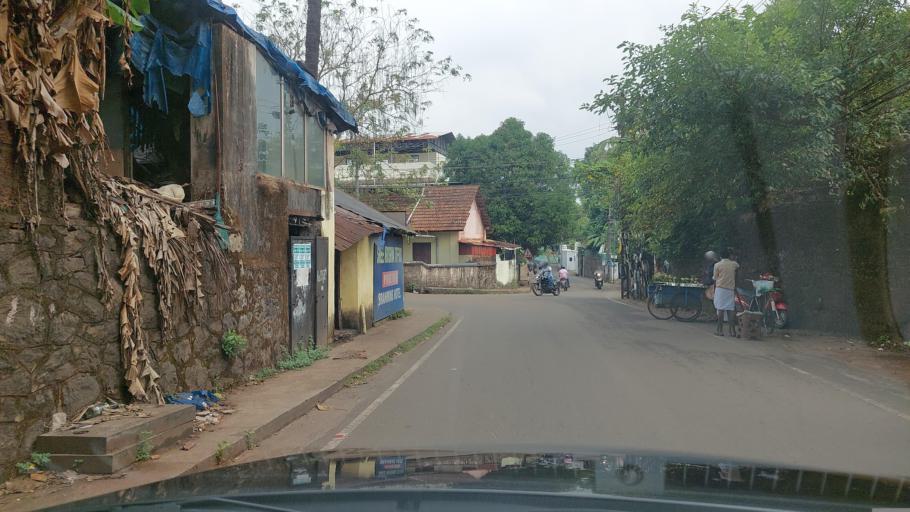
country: IN
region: Kerala
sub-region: Kozhikode
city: Kozhikode
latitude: 11.2455
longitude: 75.7882
